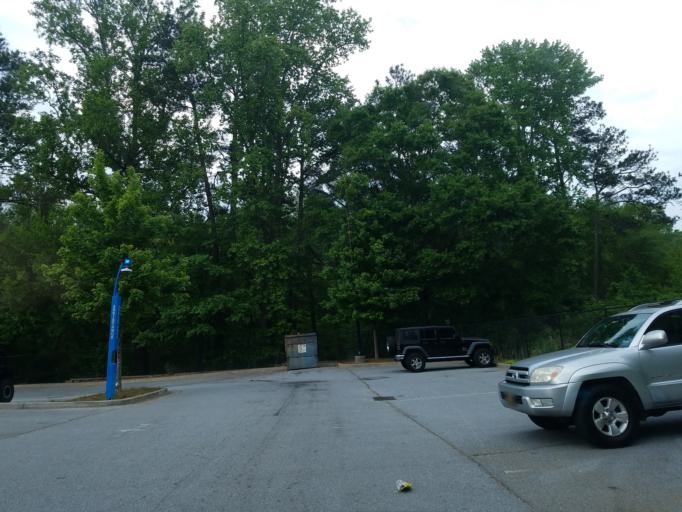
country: US
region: Georgia
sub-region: Cobb County
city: Fair Oaks
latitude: 33.9349
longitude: -84.5245
